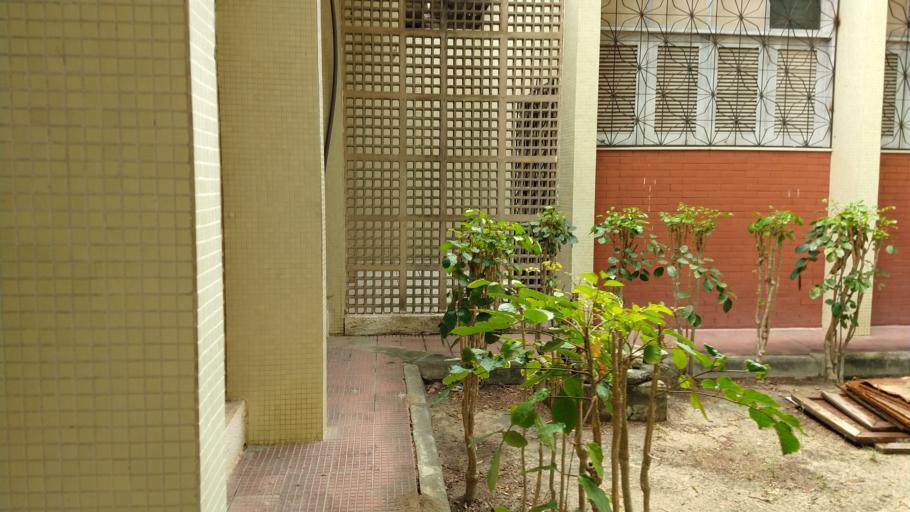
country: BR
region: Ceara
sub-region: Fortaleza
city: Fortaleza
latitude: -3.7469
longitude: -38.5741
